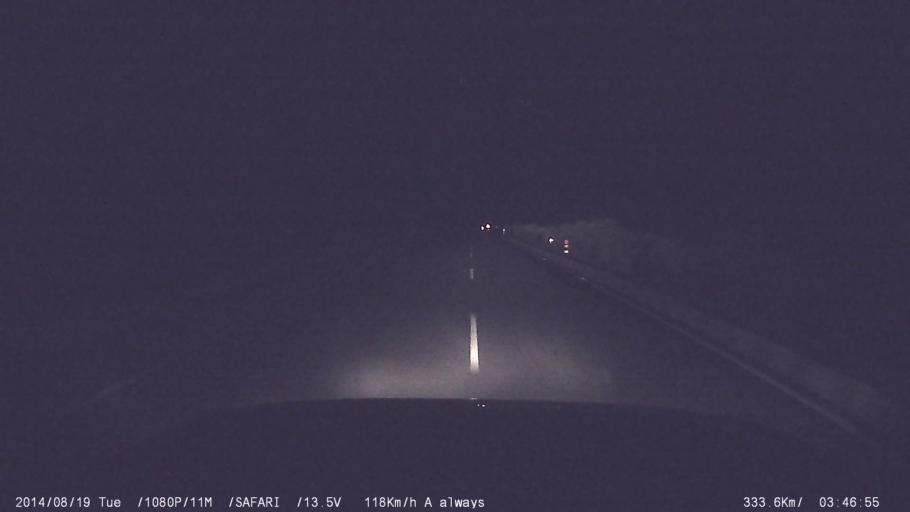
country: IN
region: Tamil Nadu
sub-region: Erode
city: Vijayapuri
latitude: 11.2352
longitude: 77.4834
